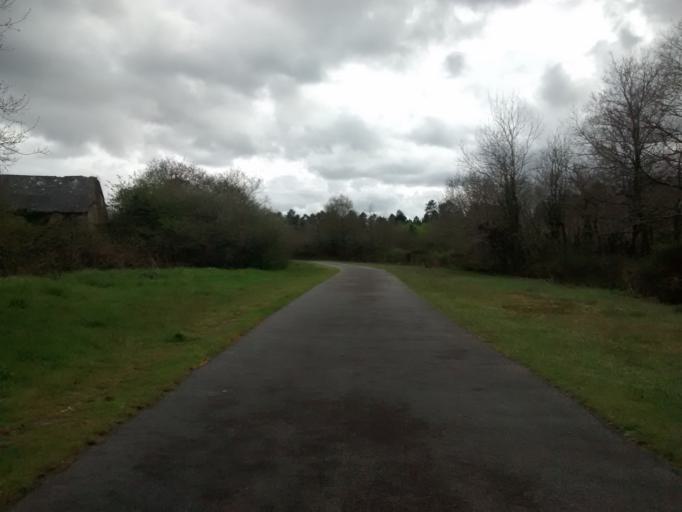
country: FR
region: Brittany
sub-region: Departement du Morbihan
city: Pleucadeuc
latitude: 47.7596
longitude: -2.3997
